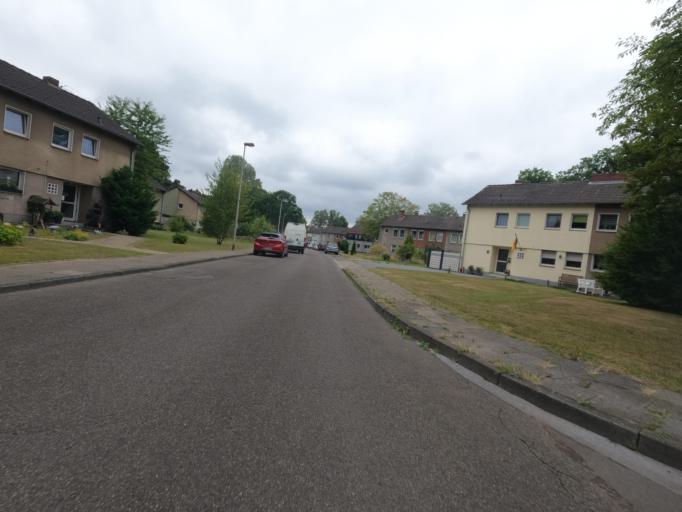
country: DE
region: North Rhine-Westphalia
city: Geilenkirchen
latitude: 50.9540
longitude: 6.0592
